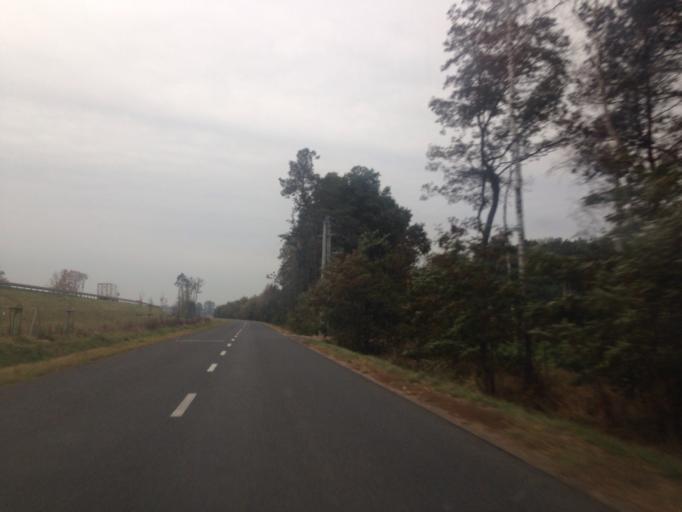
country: PL
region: Greater Poland Voivodeship
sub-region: Powiat gnieznienski
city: Lubowo
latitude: 52.4840
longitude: 17.4216
